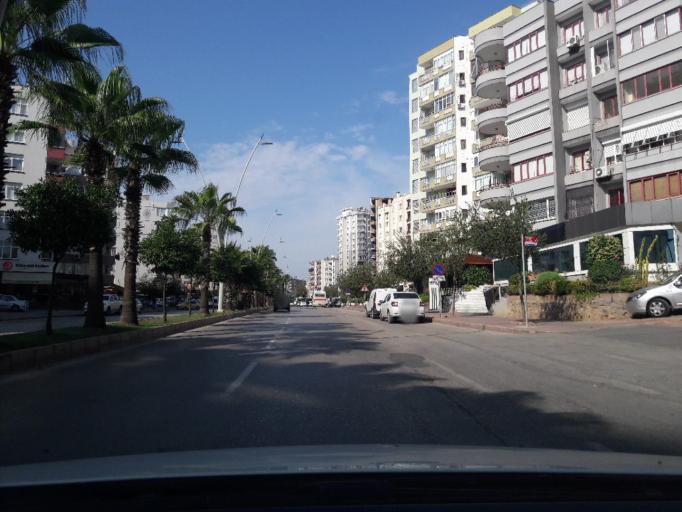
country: TR
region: Adana
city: Adana
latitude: 37.0153
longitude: 35.3246
